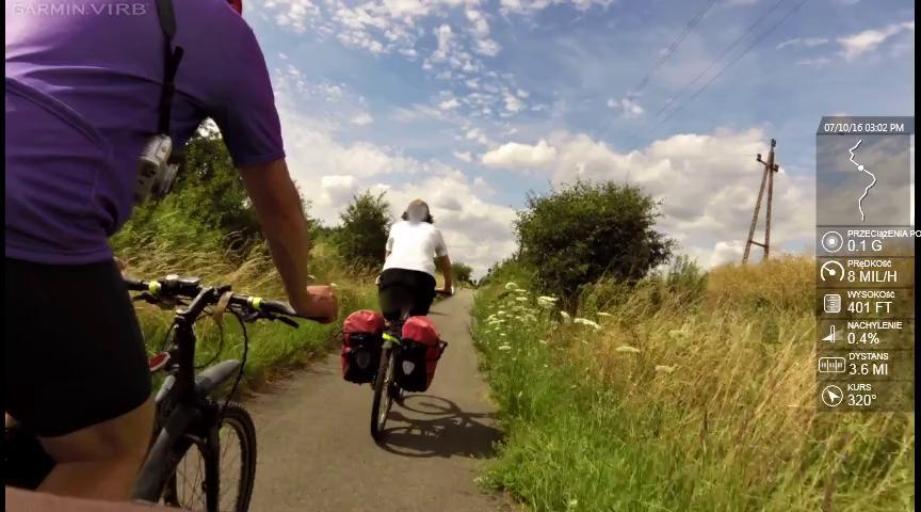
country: PL
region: West Pomeranian Voivodeship
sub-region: Powiat gryfinski
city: Banie
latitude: 53.1144
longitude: 14.6292
